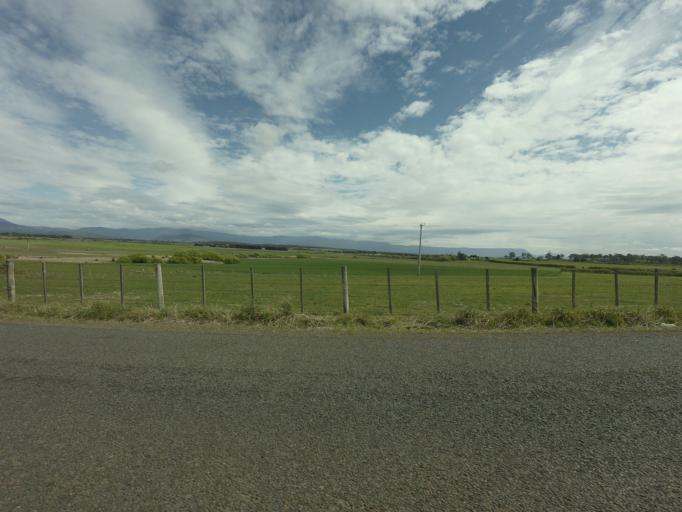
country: AU
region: Tasmania
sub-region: Northern Midlands
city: Longford
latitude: -41.7559
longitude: 147.2064
